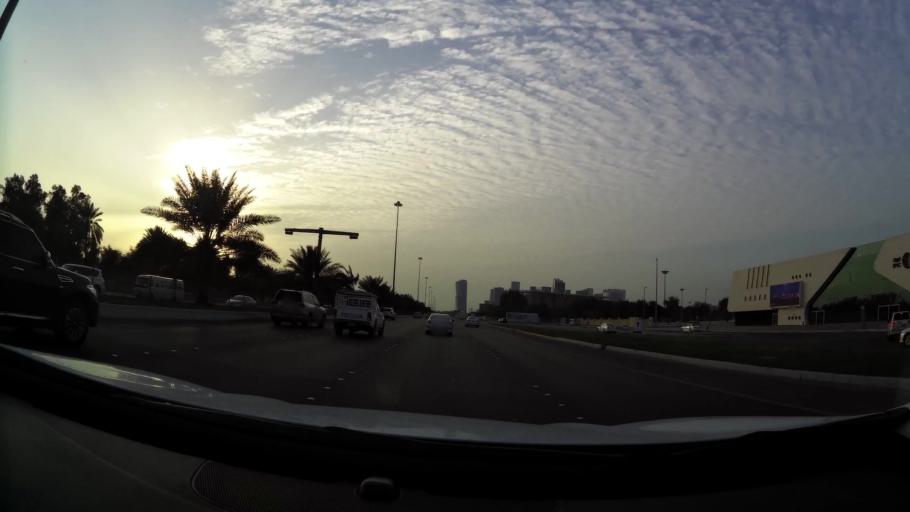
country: AE
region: Abu Dhabi
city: Abu Dhabi
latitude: 24.4125
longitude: 54.4538
